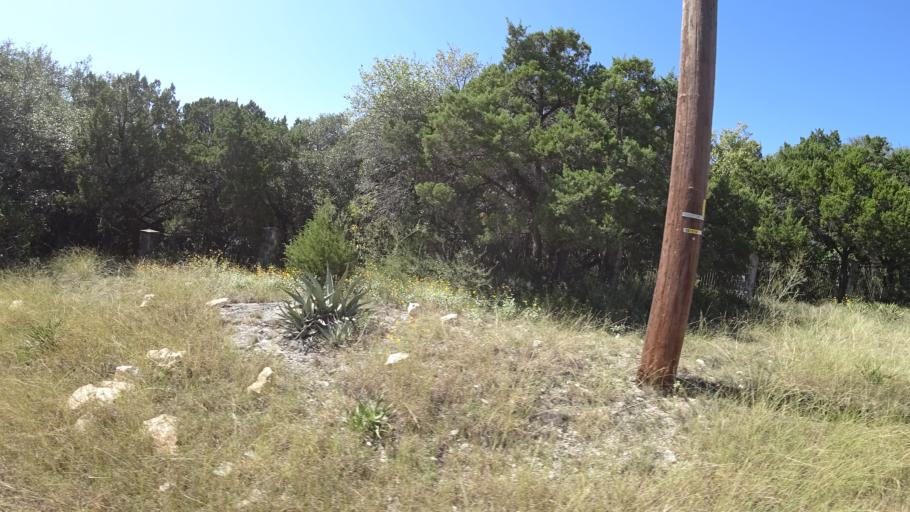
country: US
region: Texas
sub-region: Travis County
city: West Lake Hills
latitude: 30.3246
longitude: -97.7796
